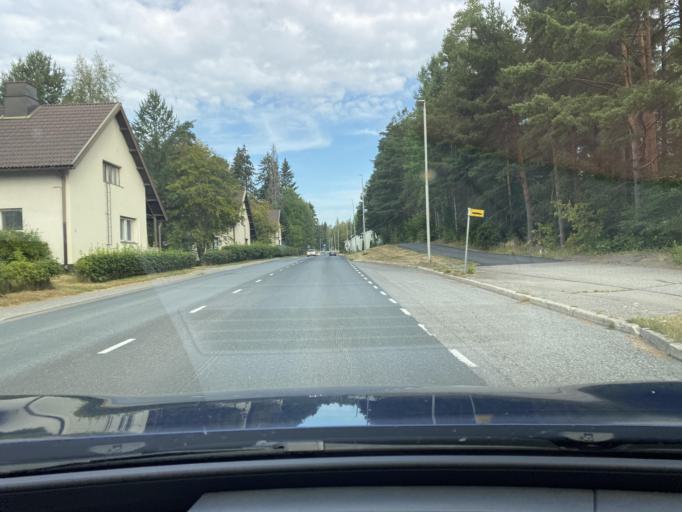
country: FI
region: Pirkanmaa
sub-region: Lounais-Pirkanmaa
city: Vammala
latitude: 61.3524
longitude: 22.8959
